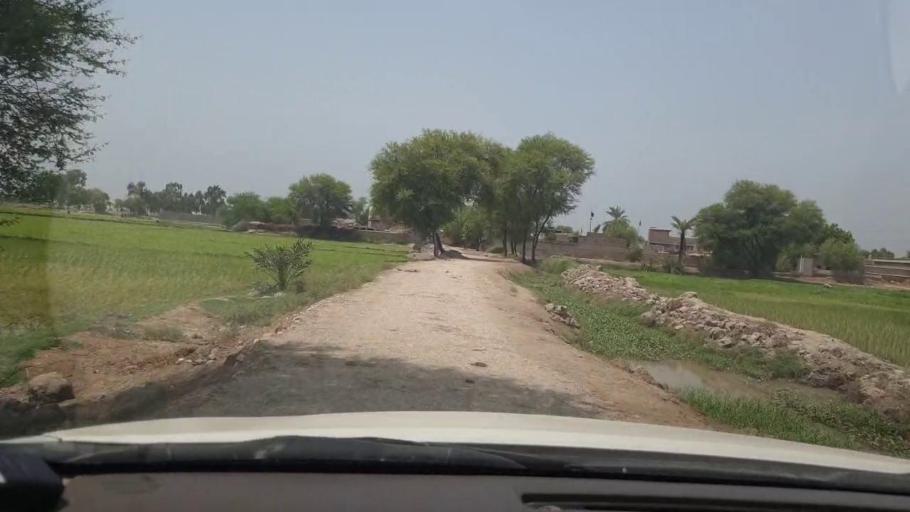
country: PK
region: Sindh
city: Garhi Yasin
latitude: 27.9493
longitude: 68.5232
